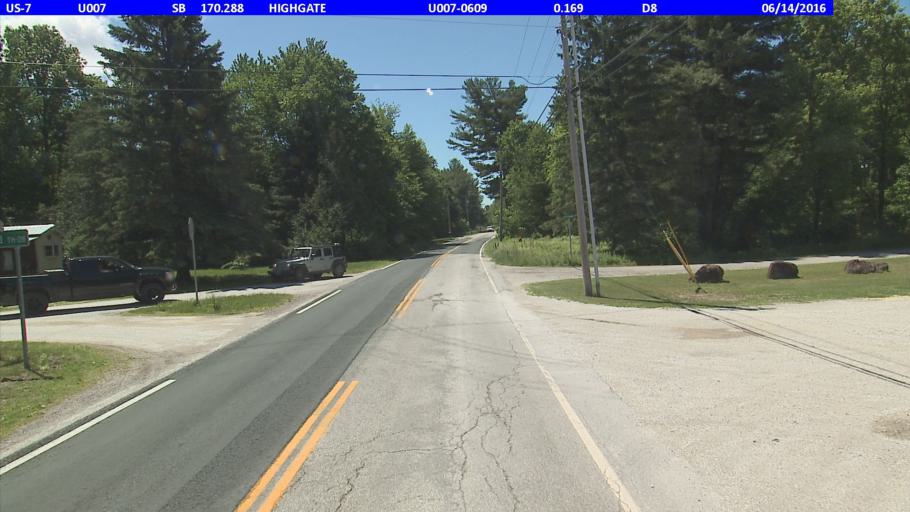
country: US
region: Vermont
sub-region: Franklin County
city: Swanton
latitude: 44.9355
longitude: -73.1186
